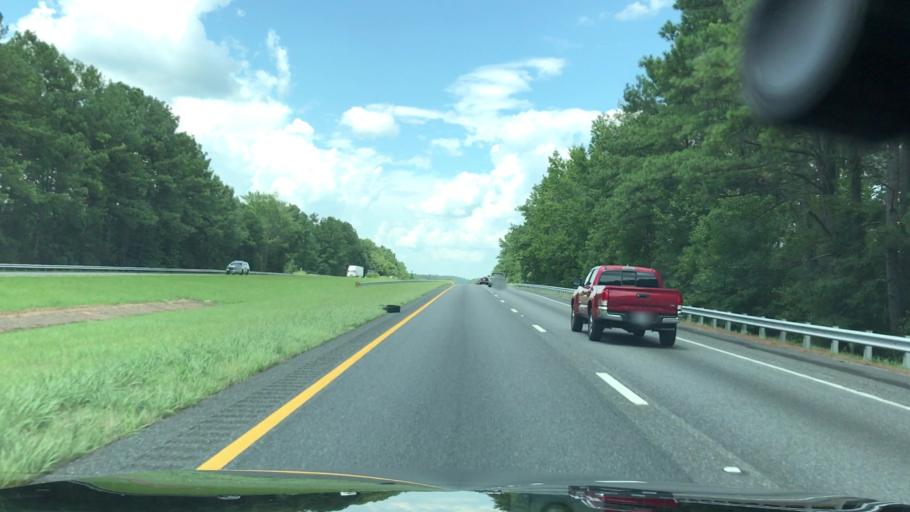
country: US
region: South Carolina
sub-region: York County
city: Lesslie
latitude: 34.7915
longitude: -81.0380
